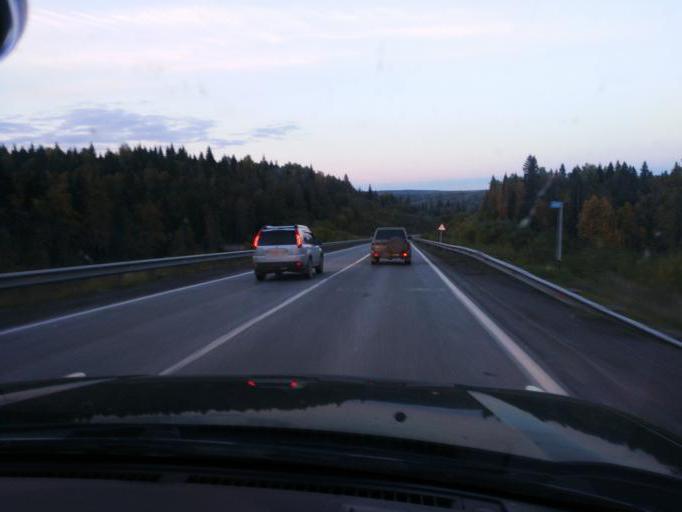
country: RU
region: Perm
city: Sylva
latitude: 58.2951
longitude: 56.7562
